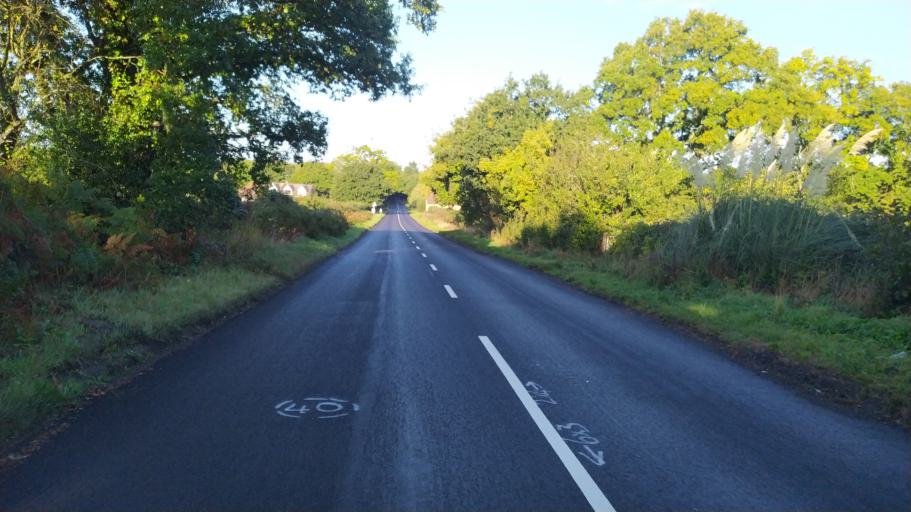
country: GB
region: England
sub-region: Dorset
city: Three Legged Cross
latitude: 50.8563
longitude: -1.9119
